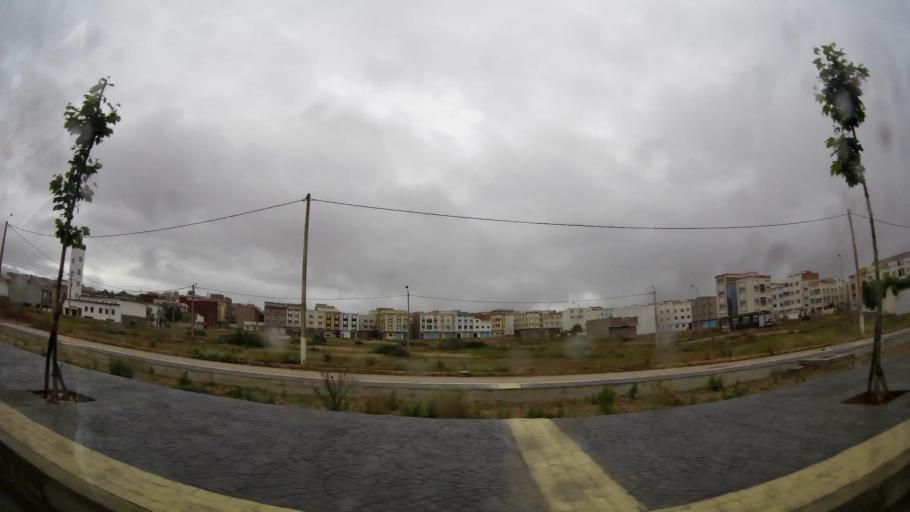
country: MA
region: Taza-Al Hoceima-Taounate
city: Imzourene
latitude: 35.1380
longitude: -3.8476
